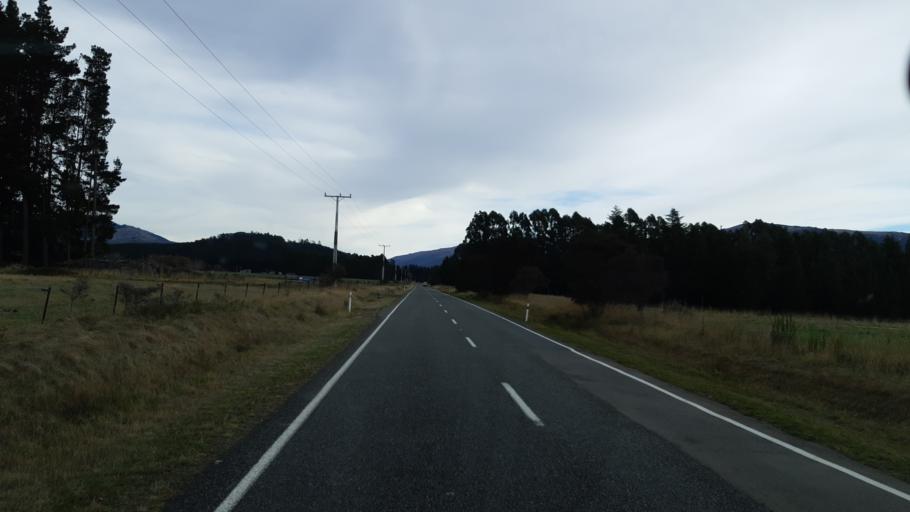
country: NZ
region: Tasman
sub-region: Tasman District
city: Brightwater
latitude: -41.6551
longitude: 173.2487
